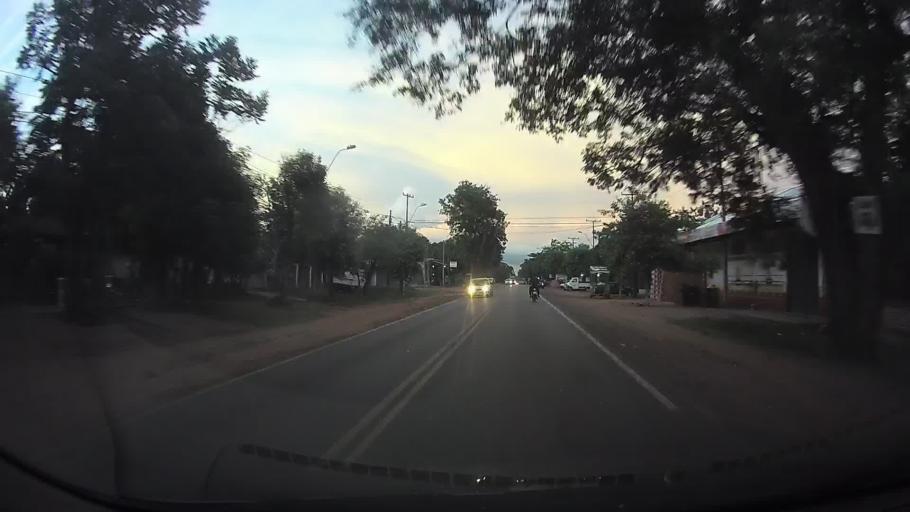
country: PY
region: Central
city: Ita
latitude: -25.5013
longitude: -57.3570
